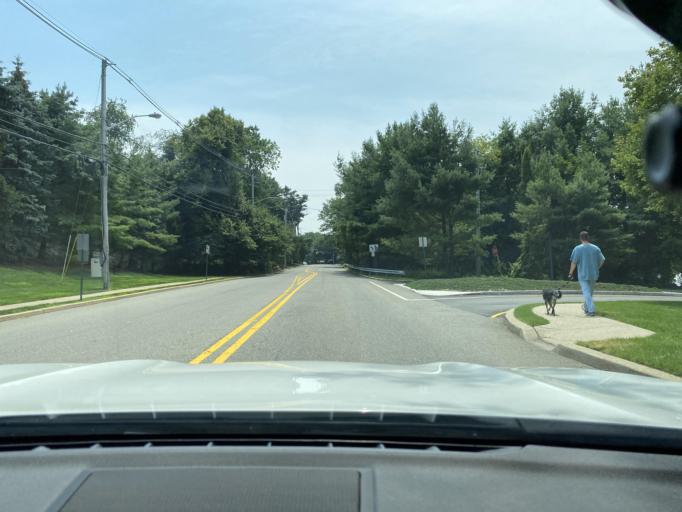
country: US
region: New Jersey
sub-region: Bergen County
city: Mahwah
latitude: 41.0849
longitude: -74.1272
